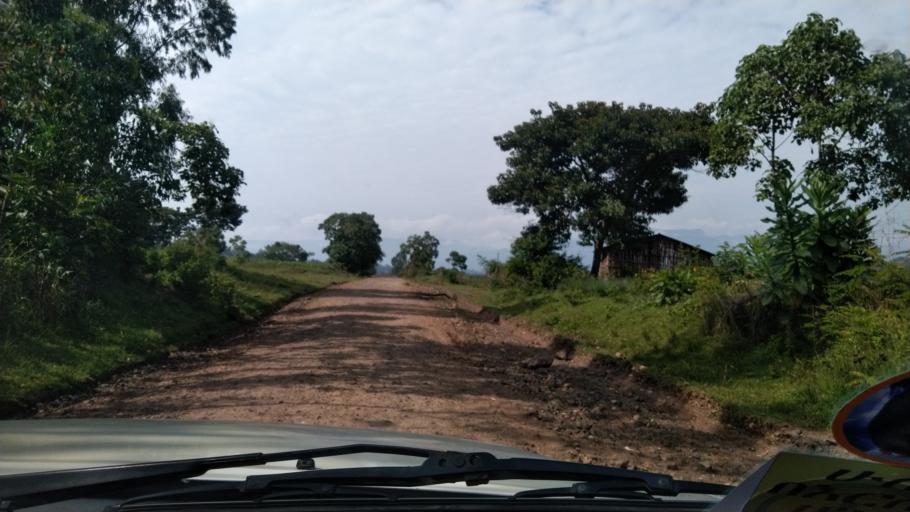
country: ET
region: Oromiya
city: Jima
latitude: 7.6796
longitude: 37.2394
